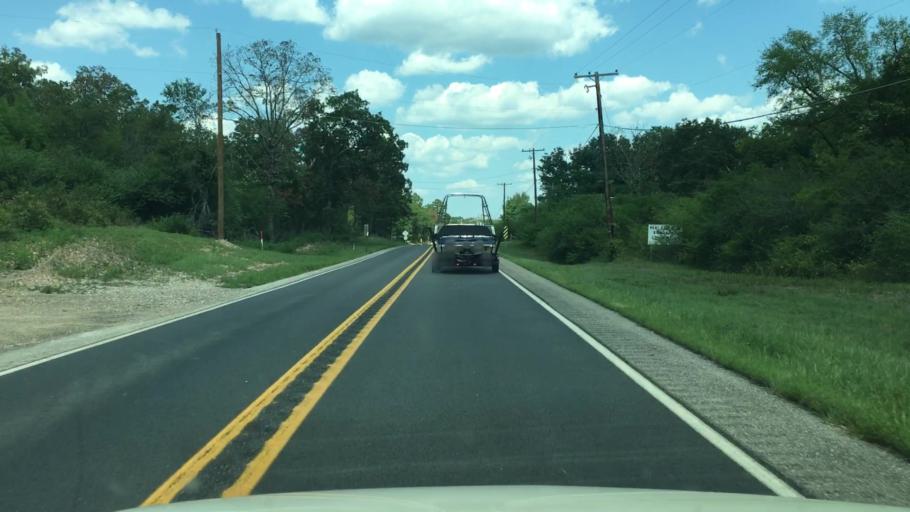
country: US
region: Arkansas
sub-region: Garland County
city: Lake Hamilton
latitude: 34.3896
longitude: -93.1198
